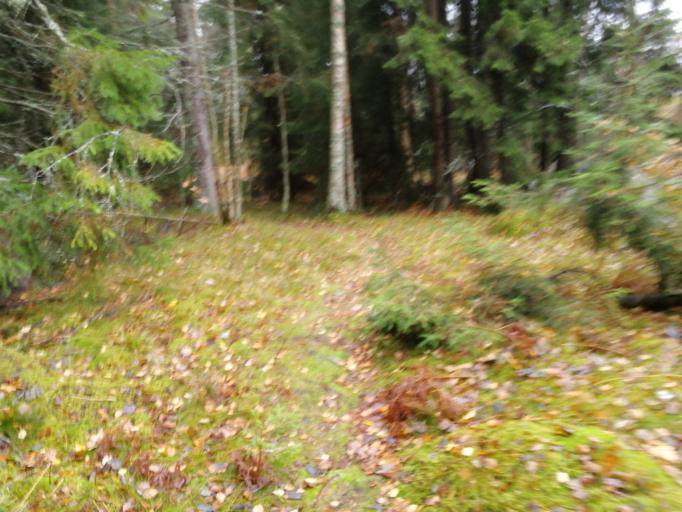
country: FI
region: Pirkanmaa
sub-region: Tampere
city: Tampere
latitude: 61.4559
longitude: 23.8849
